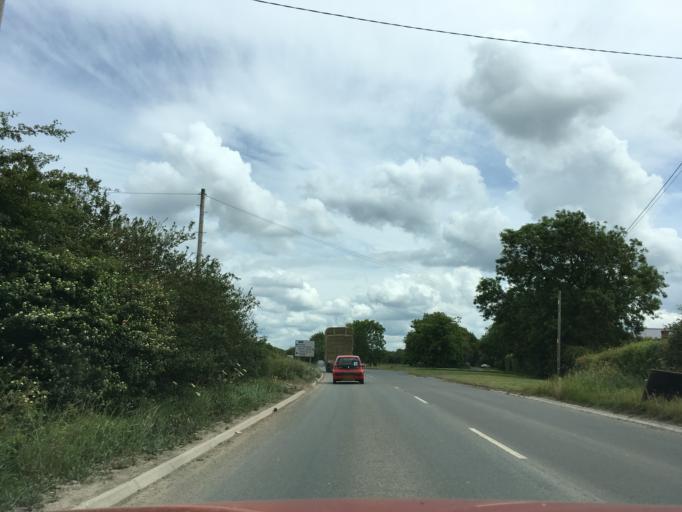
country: GB
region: England
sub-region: Wiltshire
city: Royal Wootton Bassett
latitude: 51.5598
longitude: -1.9205
